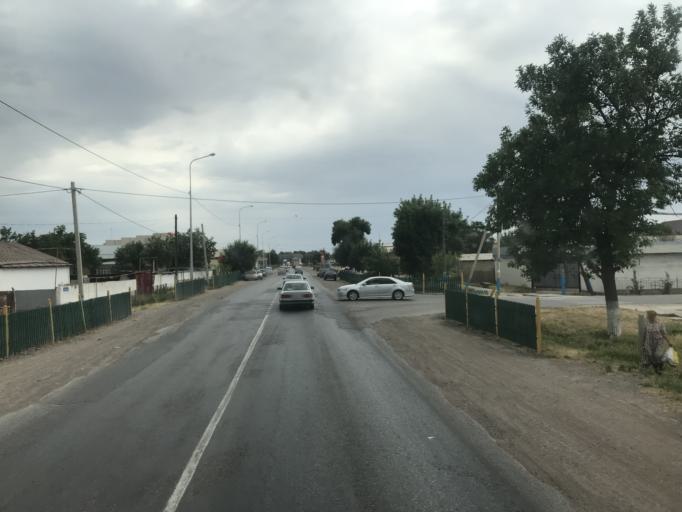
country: KZ
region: Ongtustik Qazaqstan
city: Saryaghash
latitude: 41.3469
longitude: 68.9595
